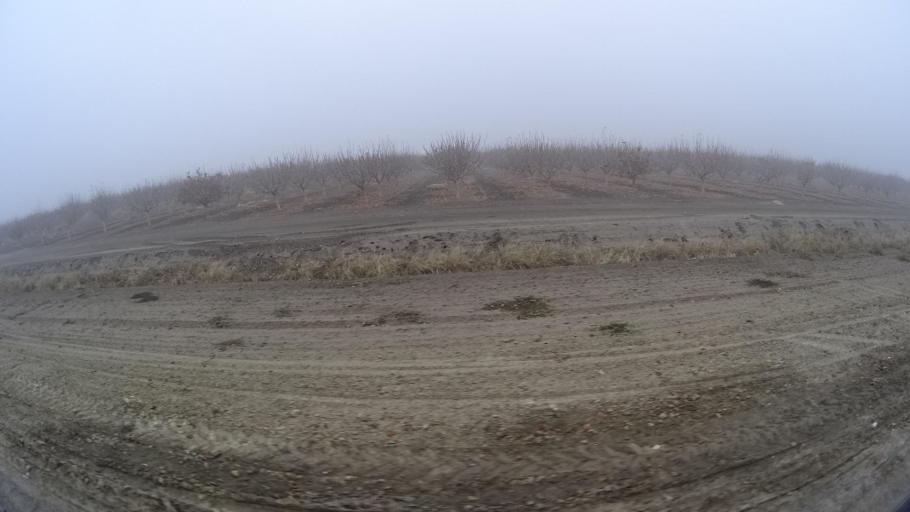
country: US
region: California
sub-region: Kern County
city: Buttonwillow
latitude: 35.4563
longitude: -119.5492
